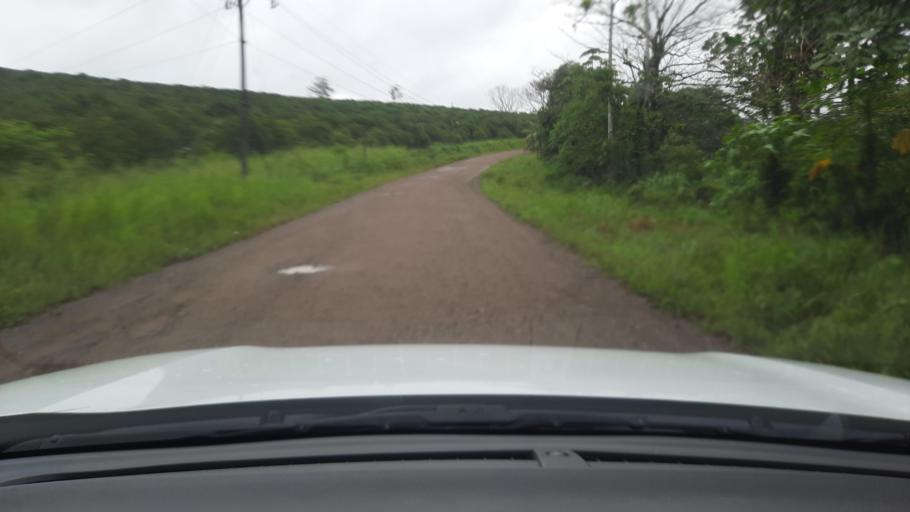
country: CR
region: Alajuela
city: San Jose
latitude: 10.9987
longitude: -85.2832
